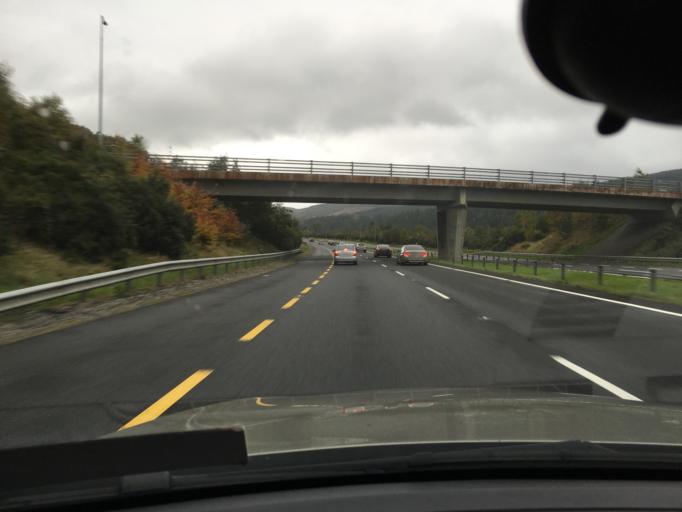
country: IE
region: Leinster
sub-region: Lu
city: Dundalk
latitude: 54.0657
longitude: -6.3520
